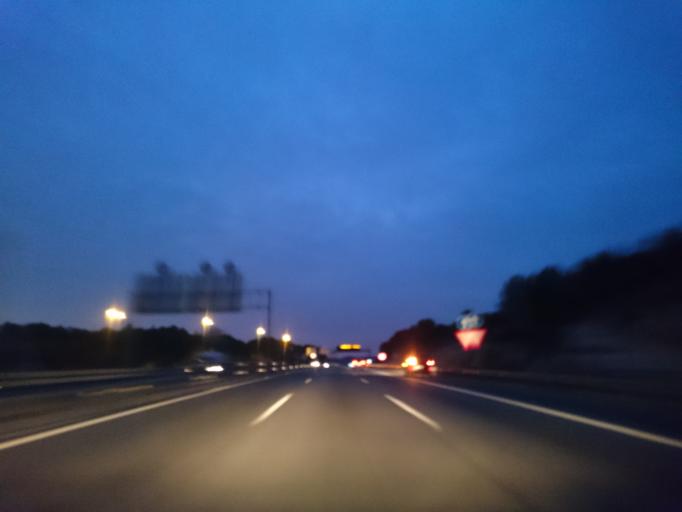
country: ES
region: Catalonia
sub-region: Provincia de Barcelona
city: Sitges
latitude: 41.2489
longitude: 1.8060
